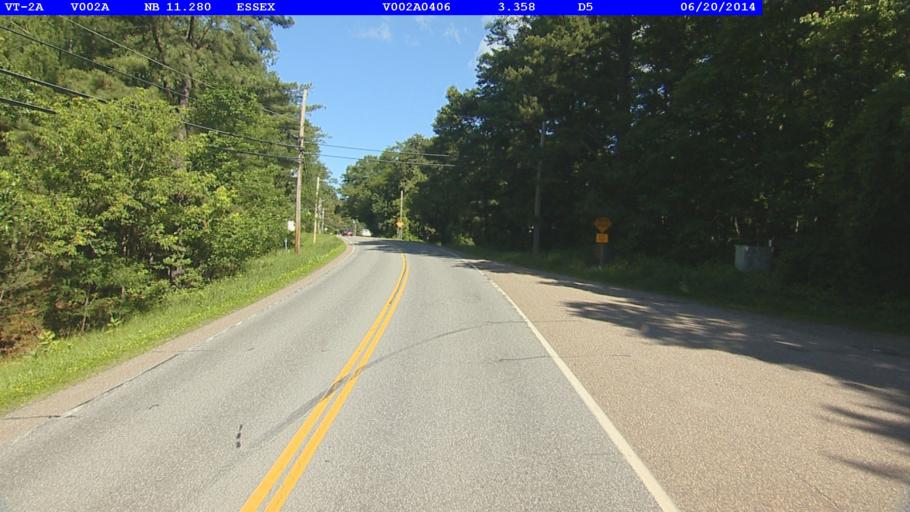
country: US
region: Vermont
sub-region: Chittenden County
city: Colchester
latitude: 44.5272
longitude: -73.1267
